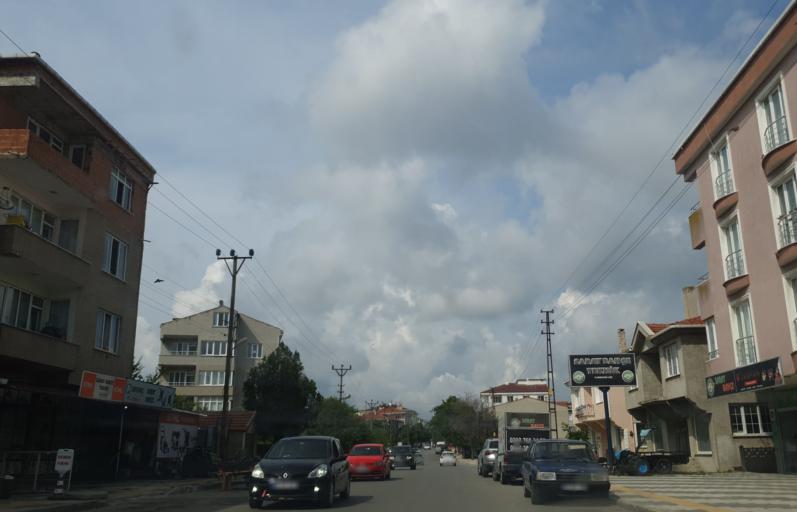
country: TR
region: Tekirdag
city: Saray
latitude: 41.4479
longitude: 27.9298
